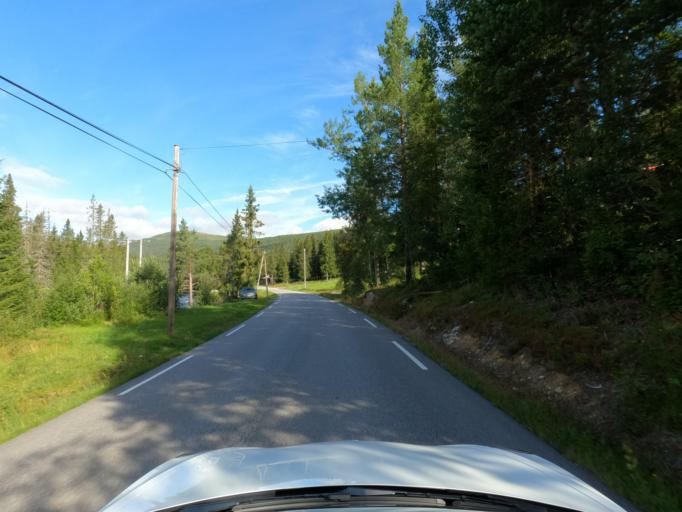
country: NO
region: Telemark
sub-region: Tinn
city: Rjukan
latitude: 60.1183
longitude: 8.7164
